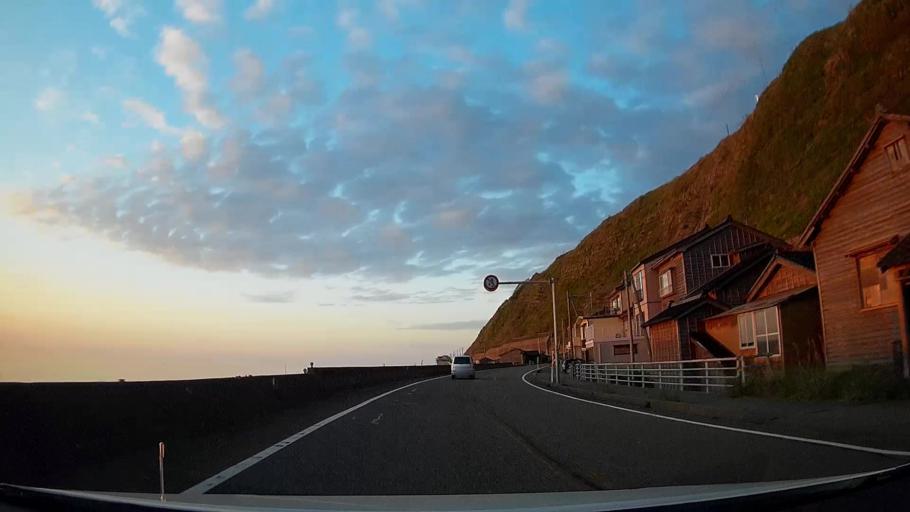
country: JP
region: Niigata
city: Joetsu
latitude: 37.1375
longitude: 138.0579
